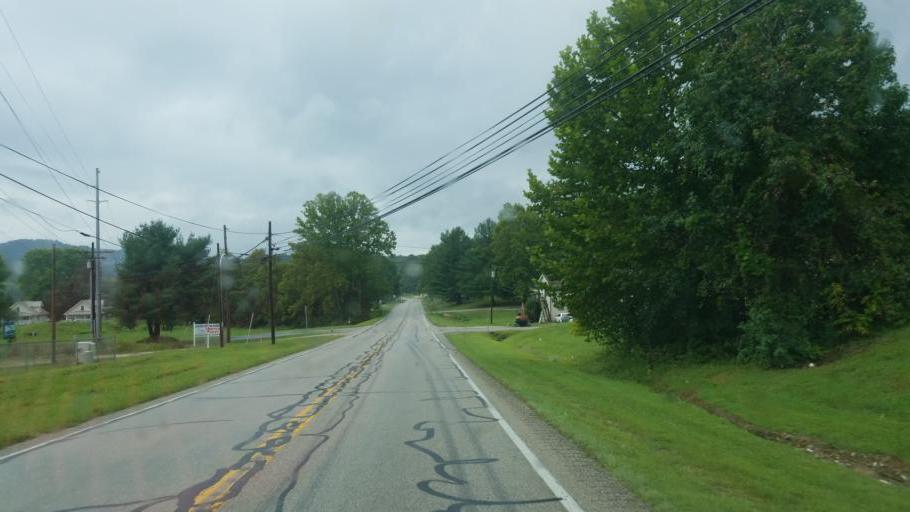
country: US
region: Kentucky
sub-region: Rowan County
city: Morehead
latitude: 38.1570
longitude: -83.4619
